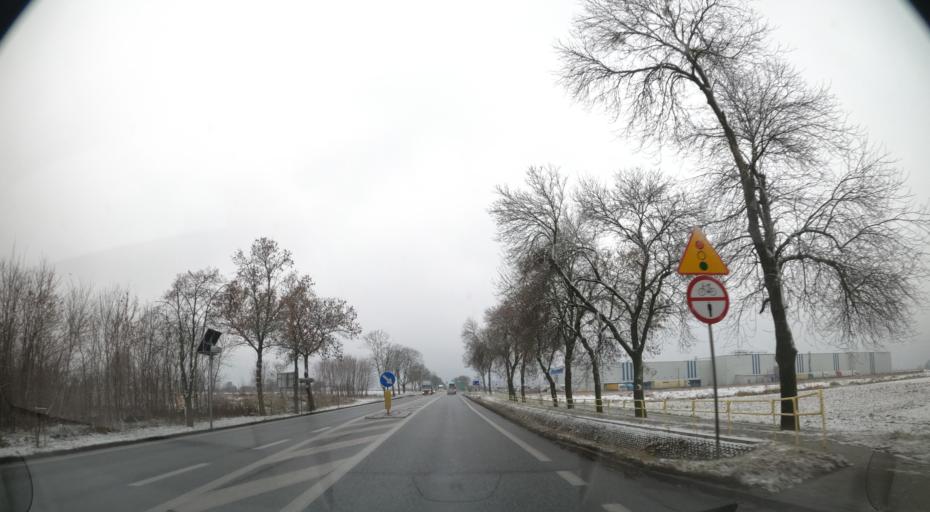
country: PL
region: Masovian Voivodeship
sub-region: Powiat warszawski zachodni
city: Jozefow
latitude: 52.2100
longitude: 20.6725
